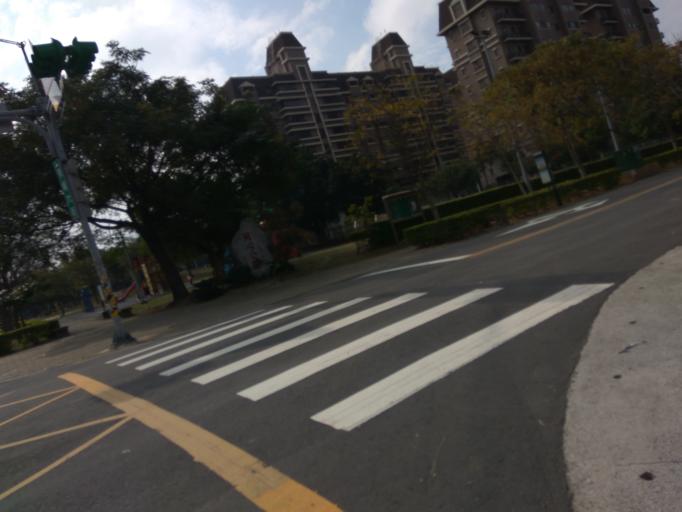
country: TW
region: Taiwan
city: Taoyuan City
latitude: 25.0051
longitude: 121.2197
